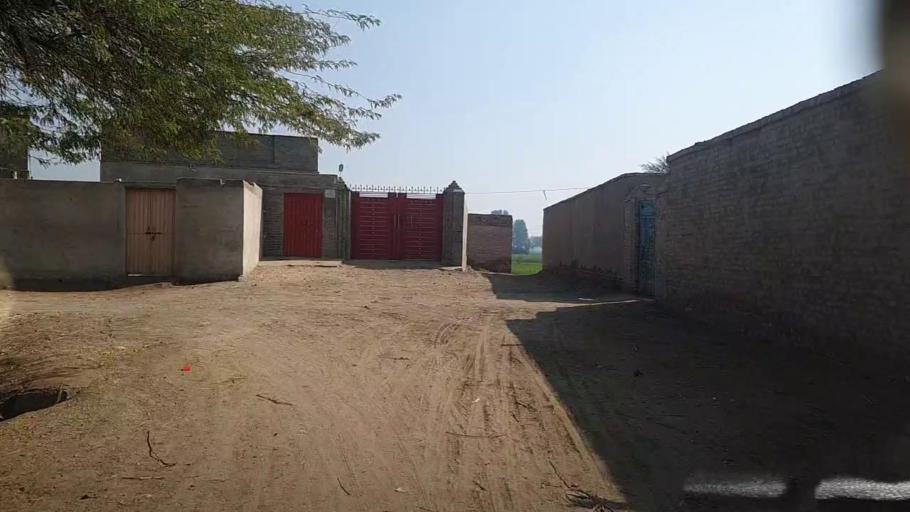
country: PK
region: Sindh
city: Khairpur
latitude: 27.9419
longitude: 69.6771
